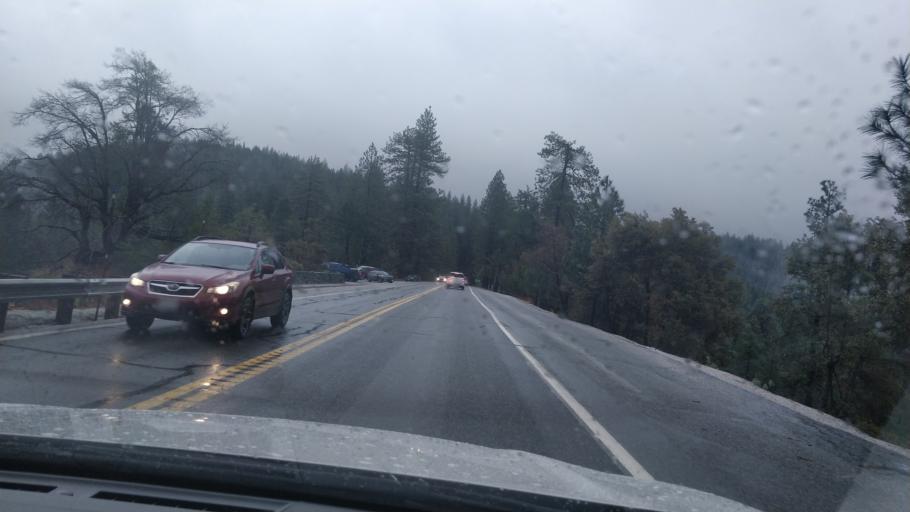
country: US
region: California
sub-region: Nevada County
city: Nevada City
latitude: 39.3176
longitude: -120.8172
